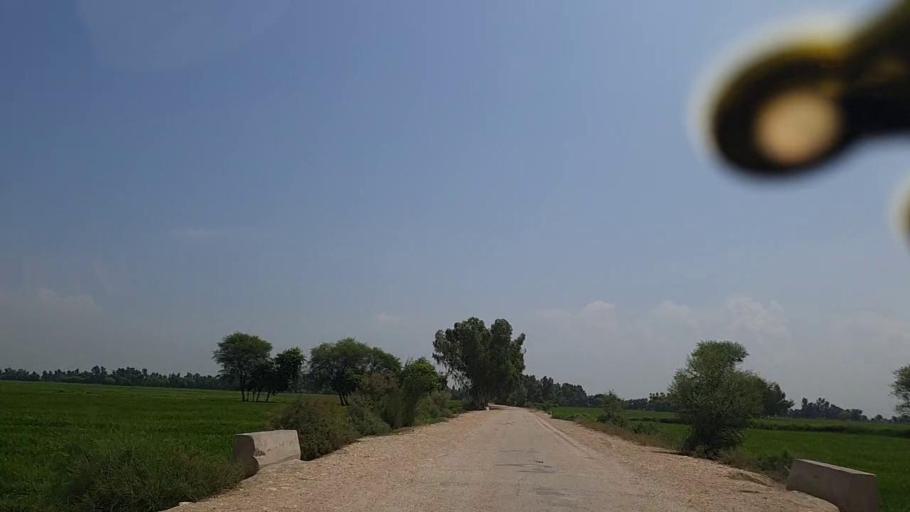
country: PK
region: Sindh
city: Rustam jo Goth
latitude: 28.1088
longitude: 68.8716
